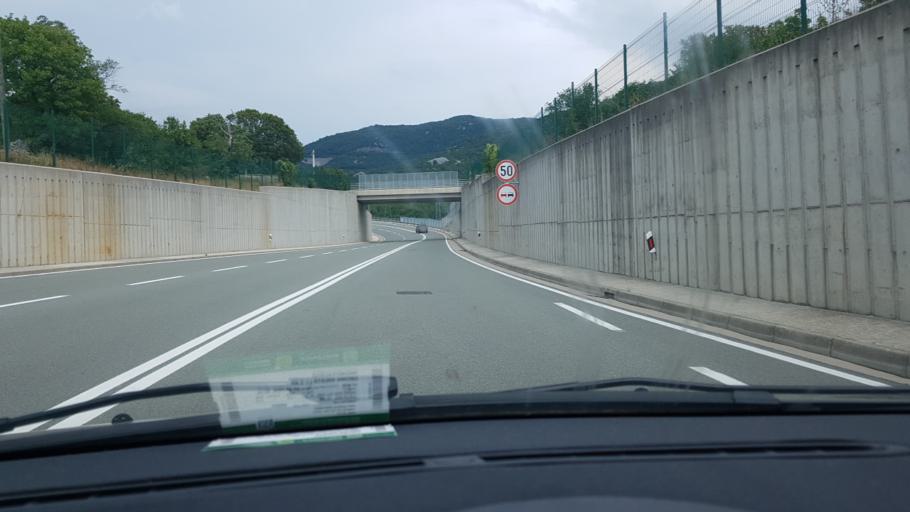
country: HR
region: Primorsko-Goranska
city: Hreljin
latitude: 45.2905
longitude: 14.5866
